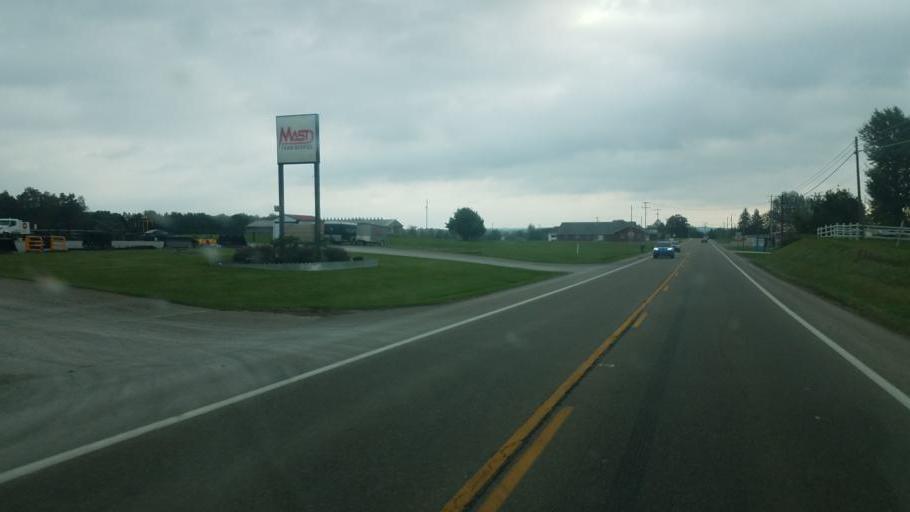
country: US
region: Ohio
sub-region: Tuscarawas County
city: Sugarcreek
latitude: 40.5462
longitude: -81.7496
